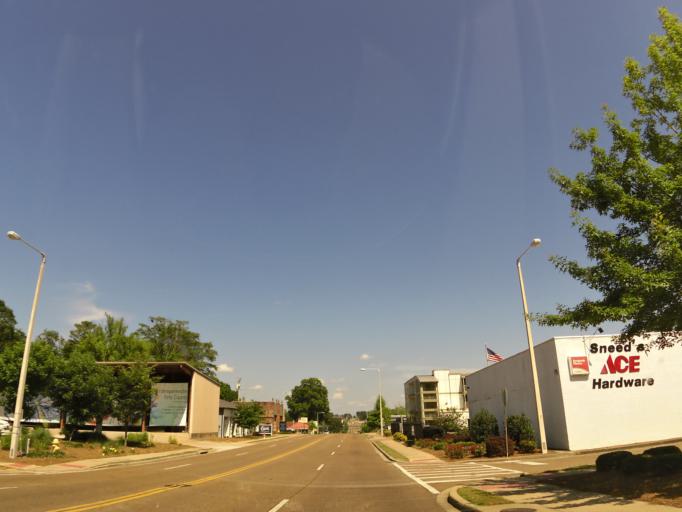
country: US
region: Mississippi
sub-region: Lafayette County
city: Oxford
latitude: 34.3638
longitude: -89.5179
